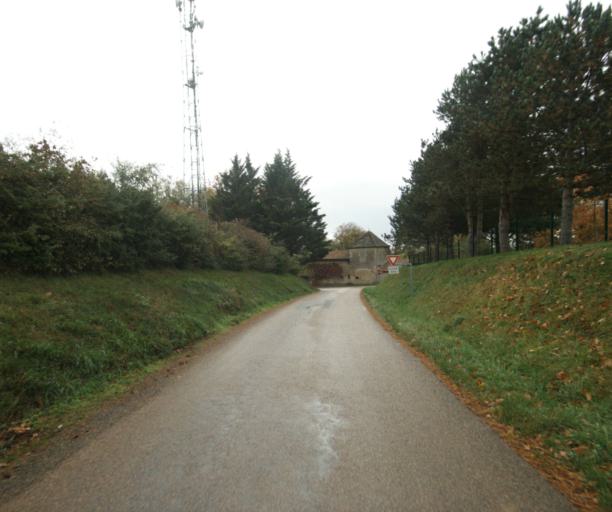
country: FR
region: Rhone-Alpes
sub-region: Departement de l'Ain
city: Pont-de-Vaux
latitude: 46.4778
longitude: 4.8752
